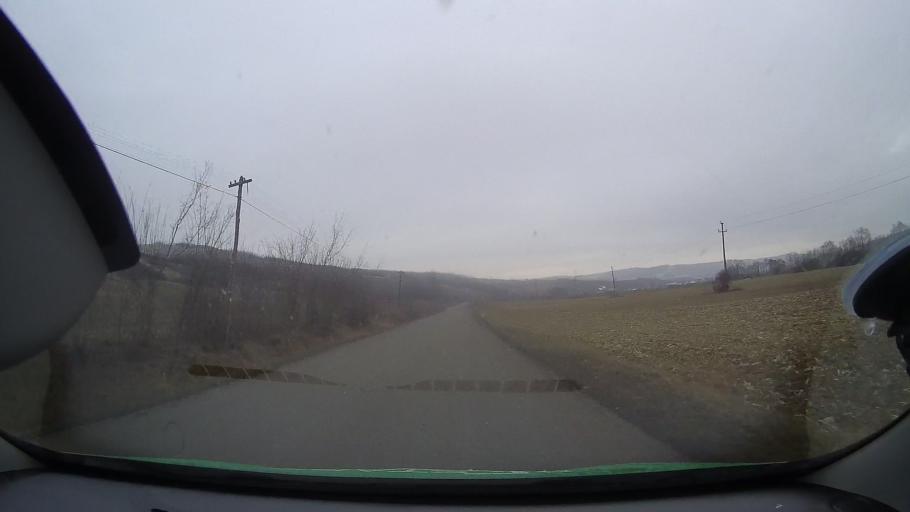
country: RO
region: Alba
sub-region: Comuna Farau
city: Farau
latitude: 46.3362
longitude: 23.9826
